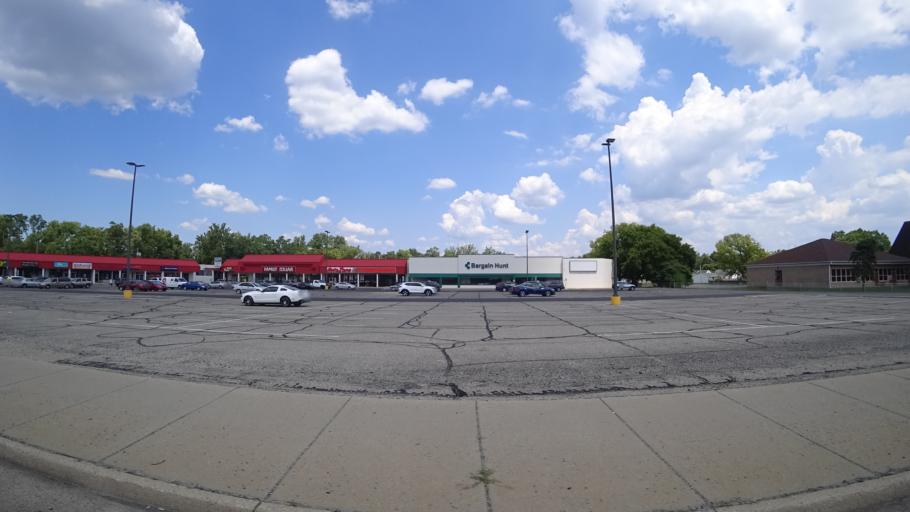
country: US
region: Ohio
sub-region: Butler County
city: Hamilton
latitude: 39.4172
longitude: -84.5861
